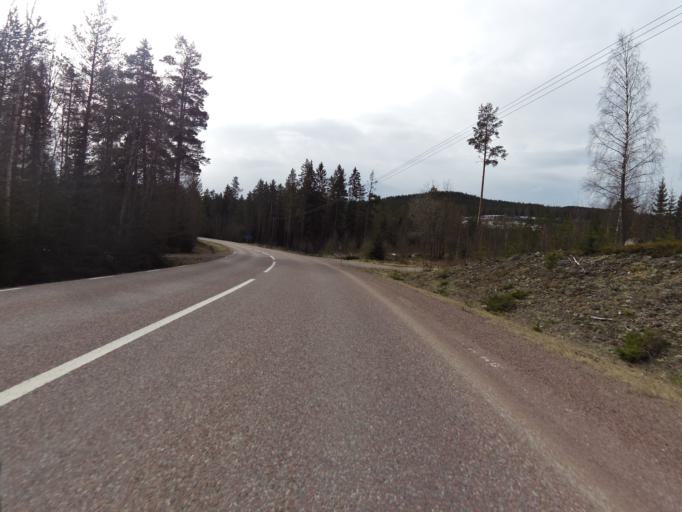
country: SE
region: Dalarna
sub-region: Hedemora Kommun
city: Langshyttan
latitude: 60.5494
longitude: 16.1229
